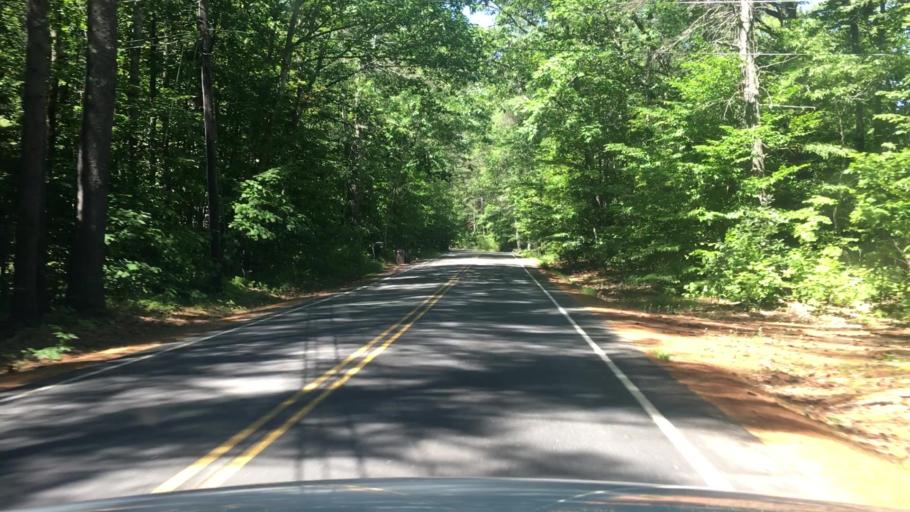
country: US
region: New Hampshire
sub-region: Merrimack County
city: Hopkinton
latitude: 43.2321
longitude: -71.6462
